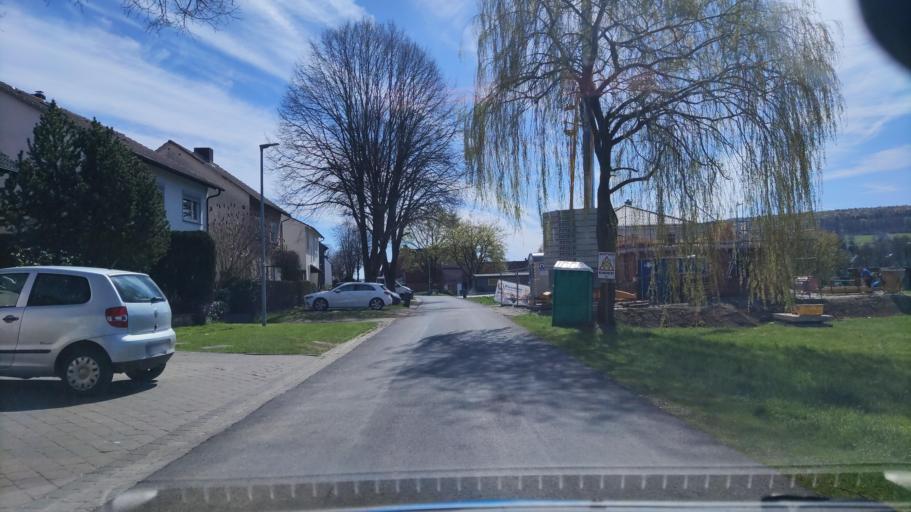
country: DE
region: Lower Saxony
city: Bodenfelde
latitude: 51.6961
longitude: 9.5572
